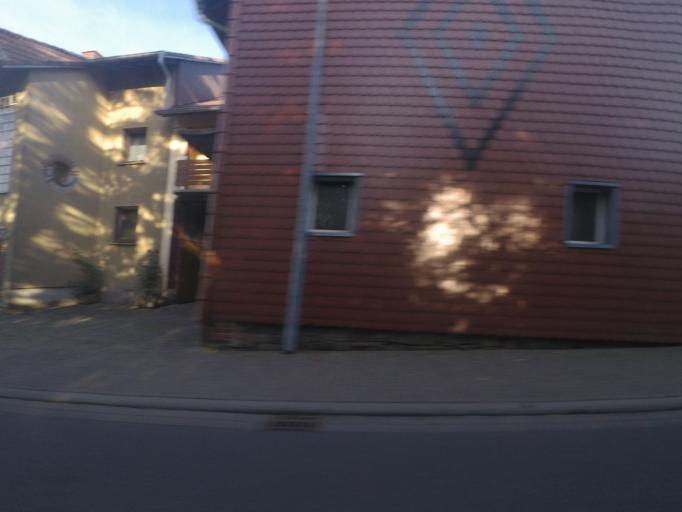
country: DE
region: Hesse
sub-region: Regierungsbezirk Darmstadt
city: Birstein
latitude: 50.3063
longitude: 9.2683
